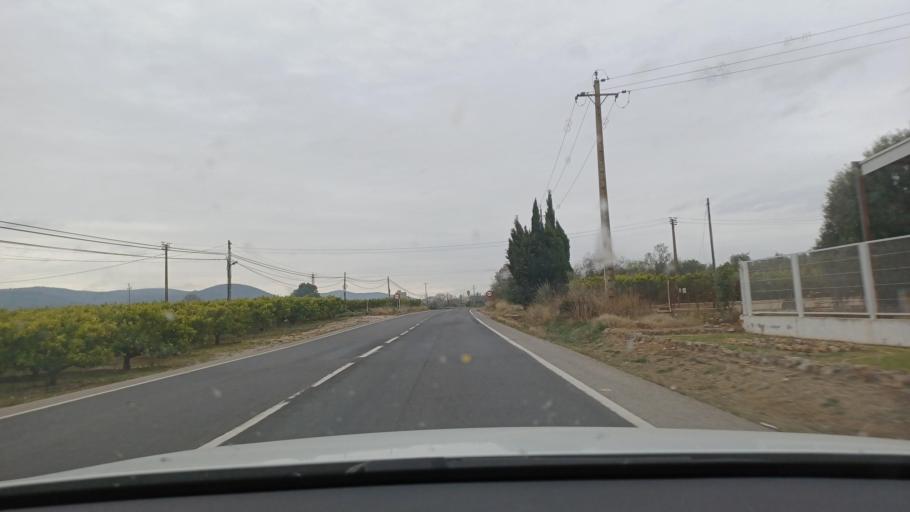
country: ES
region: Catalonia
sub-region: Provincia de Tarragona
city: Santa Barbara
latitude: 40.6881
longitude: 0.4703
